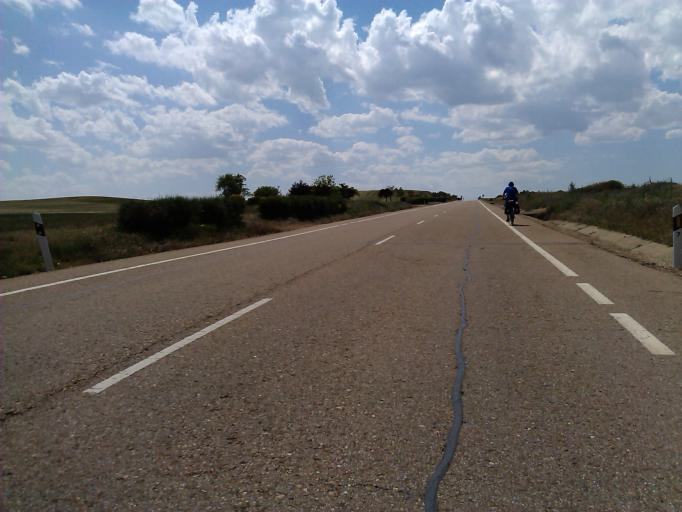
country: ES
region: Castille and Leon
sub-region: Provincia de Palencia
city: Moratinos
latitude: 42.3629
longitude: -4.9182
